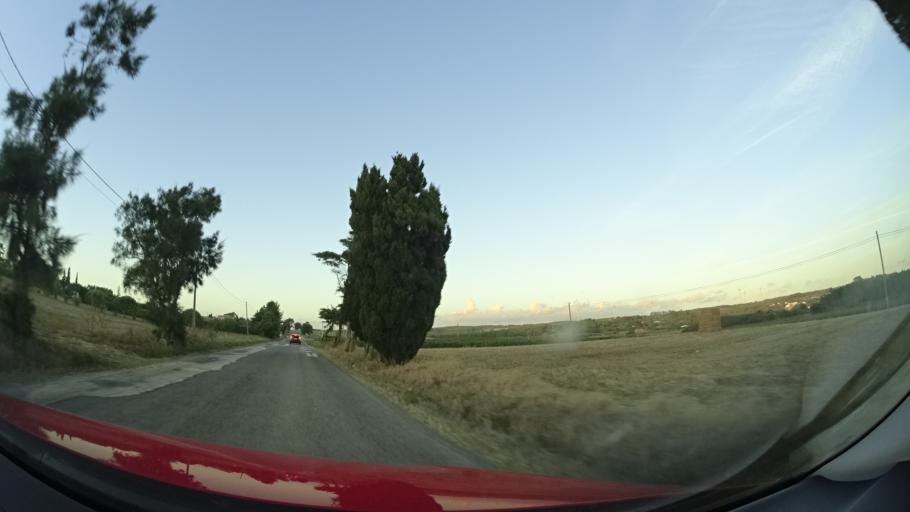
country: PT
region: Faro
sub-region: Aljezur
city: Aljezur
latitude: 37.2279
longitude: -8.8314
